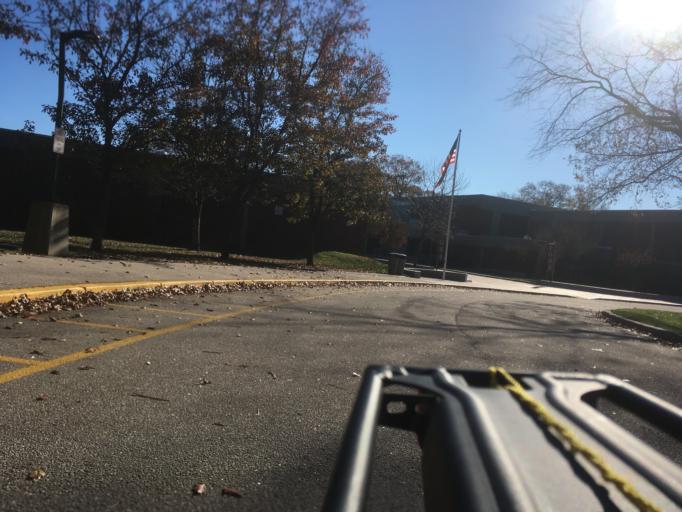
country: US
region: Rhode Island
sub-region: Kent County
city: East Greenwich
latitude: 41.6393
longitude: -71.4844
